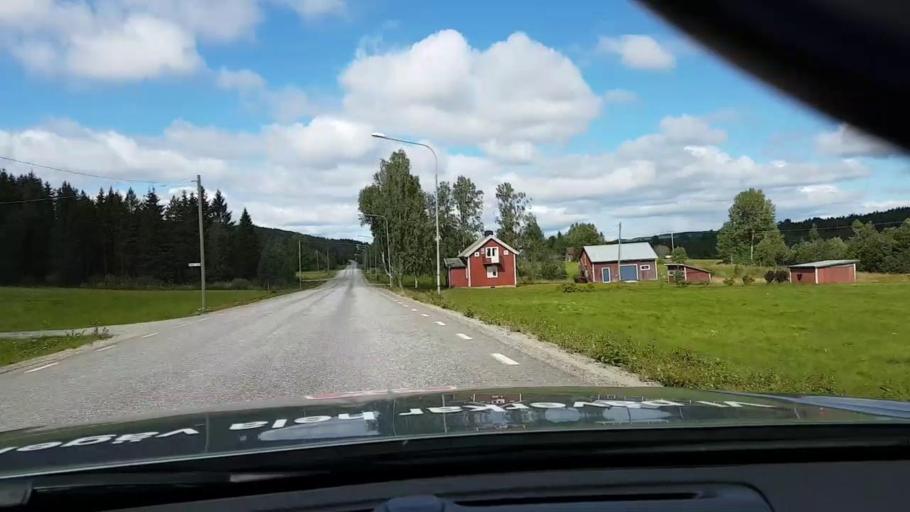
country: SE
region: Vaesternorrland
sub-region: OErnskoeldsviks Kommun
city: Bredbyn
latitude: 63.4801
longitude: 18.0918
